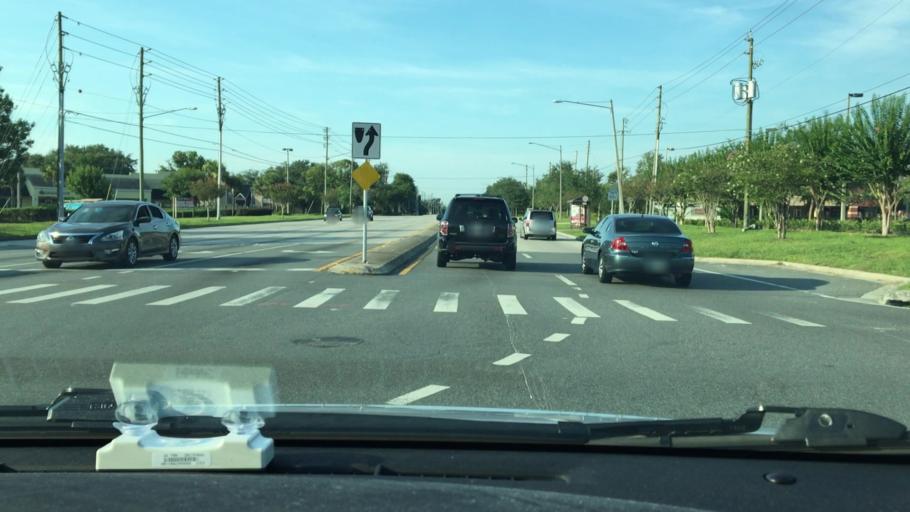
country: US
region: Florida
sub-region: Seminole County
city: Goldenrod
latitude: 28.5973
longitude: -81.2866
